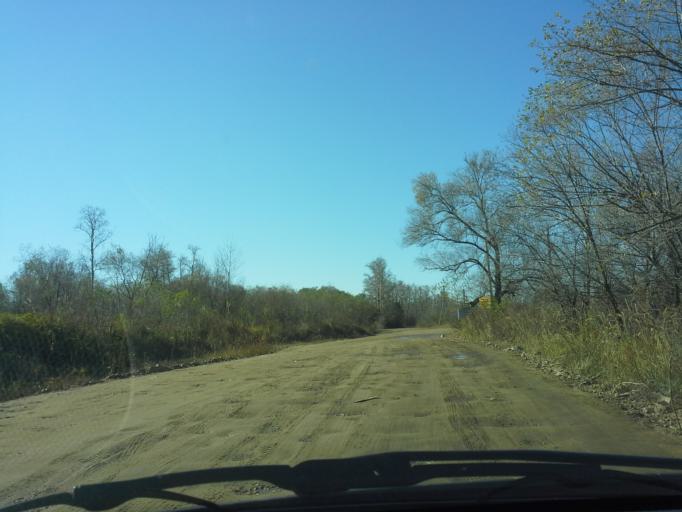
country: RU
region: Jewish Autonomous Oblast
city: Priamurskiy
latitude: 48.5395
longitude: 134.9771
